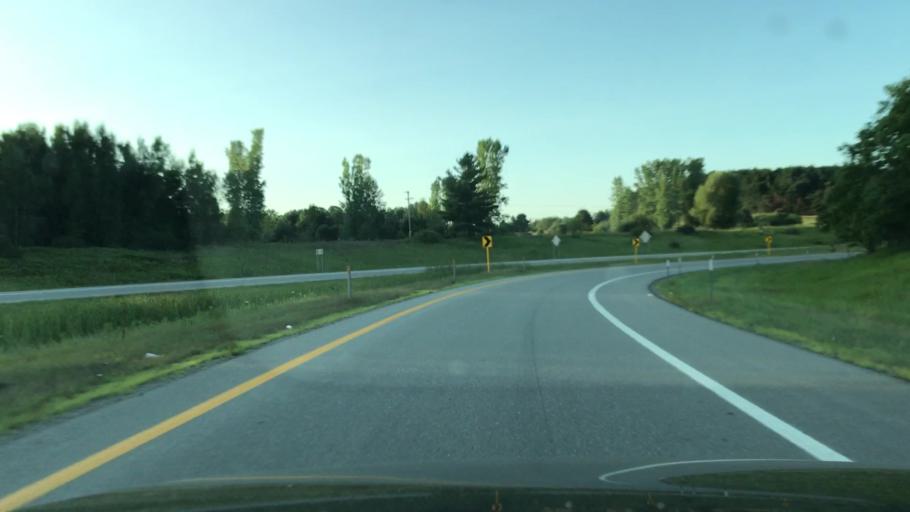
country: US
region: Michigan
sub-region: Osceola County
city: Reed City
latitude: 43.8899
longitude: -85.5317
